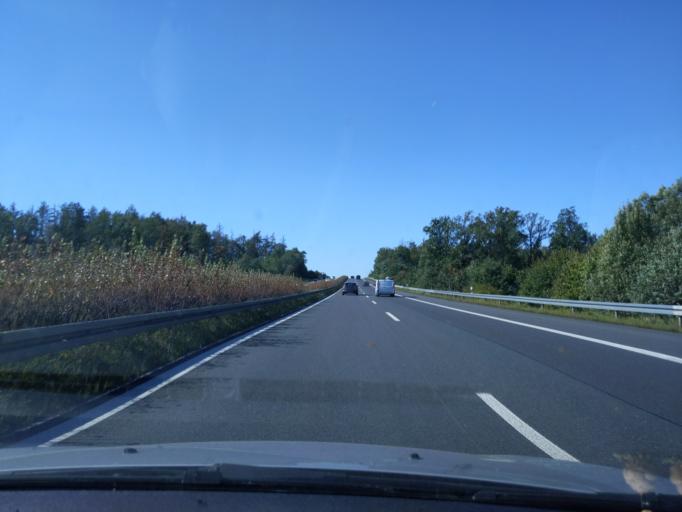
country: DE
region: Saxony
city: Wachau
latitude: 51.1713
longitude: 13.8844
